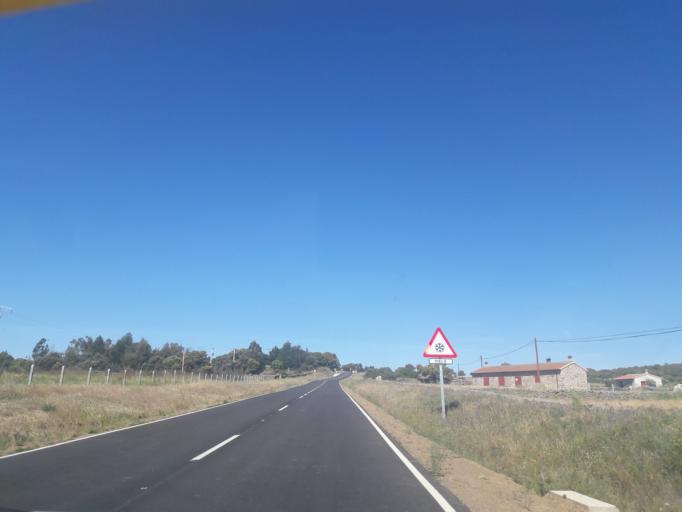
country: ES
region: Castille and Leon
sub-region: Provincia de Salamanca
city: Santibanez de Bejar
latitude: 40.4810
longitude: -5.6352
